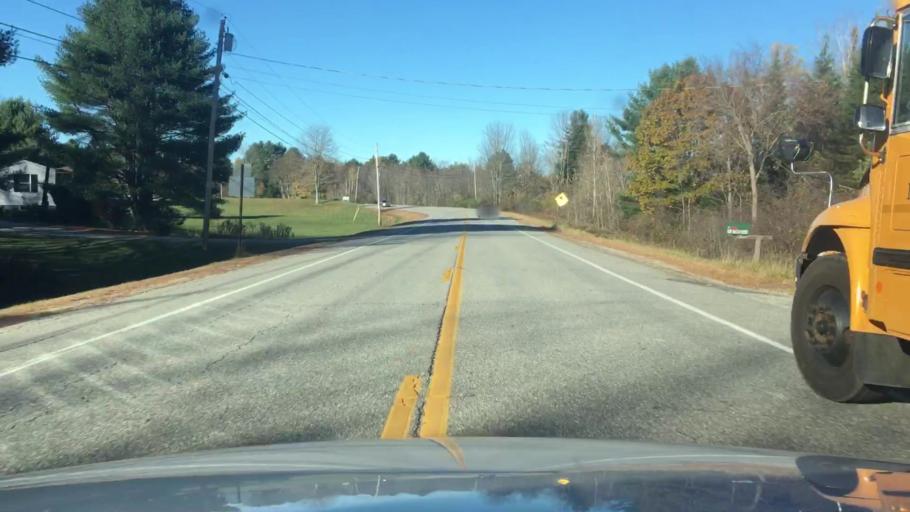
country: US
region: Maine
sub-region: Sagadahoc County
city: Topsham
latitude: 44.0214
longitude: -69.9214
